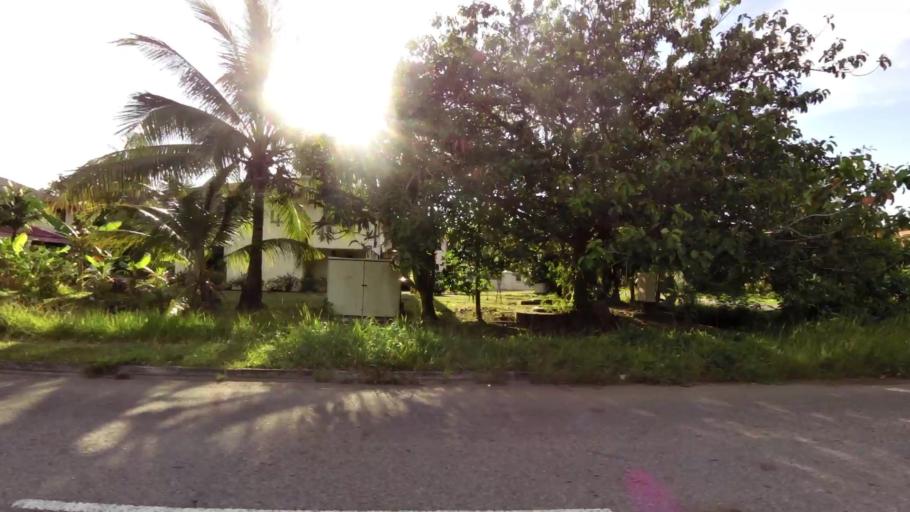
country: BN
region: Brunei and Muara
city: Bandar Seri Begawan
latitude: 4.9824
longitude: 114.9687
